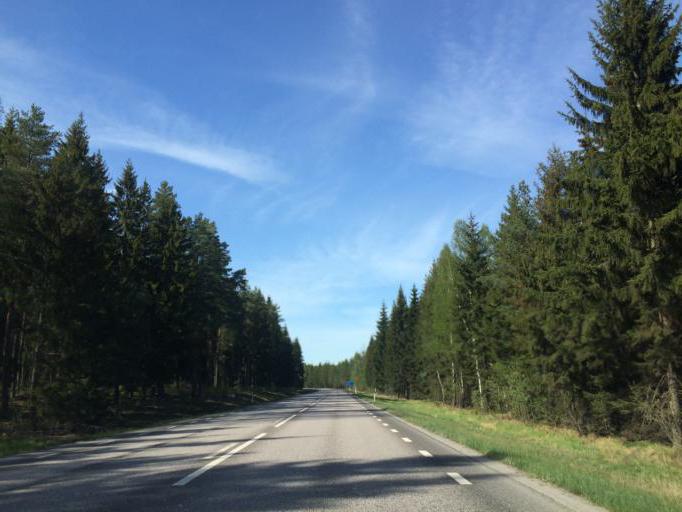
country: SE
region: Soedermanland
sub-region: Katrineholms Kommun
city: Katrineholm
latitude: 59.0661
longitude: 16.2246
